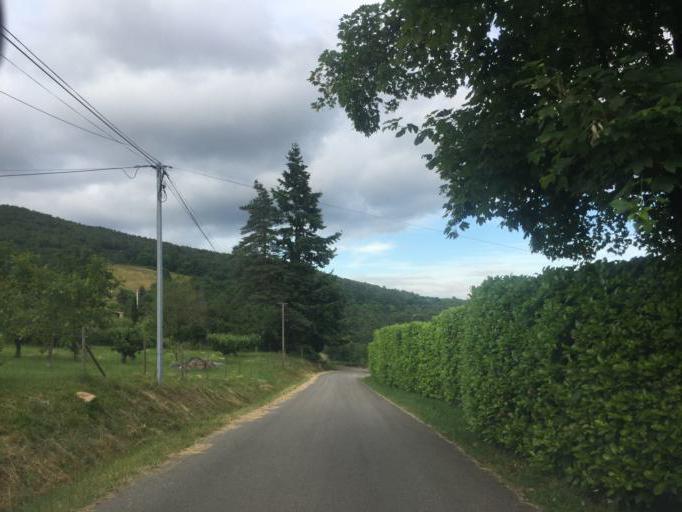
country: FR
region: Rhone-Alpes
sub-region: Departement de l'Ardeche
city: Privas
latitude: 44.7577
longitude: 4.5982
